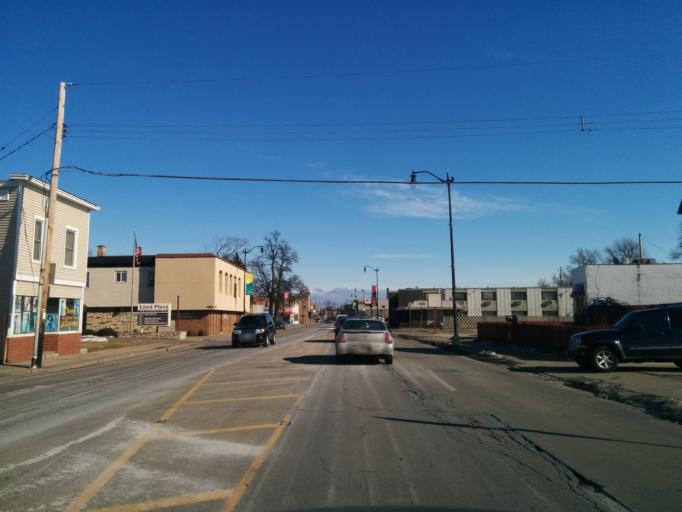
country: US
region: Wisconsin
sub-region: Racine County
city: Racine
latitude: 42.7145
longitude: -87.8015
